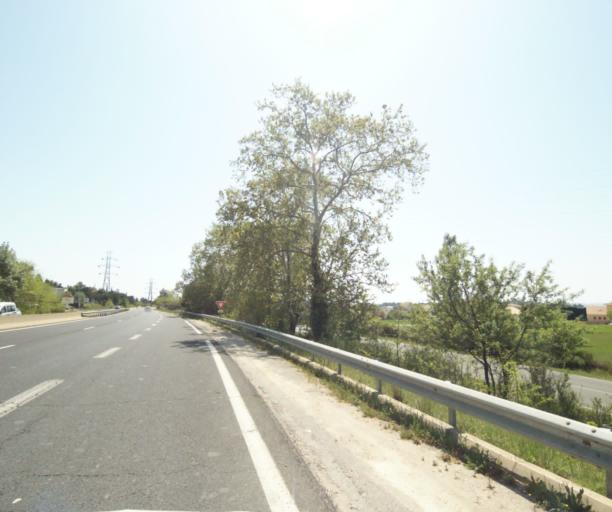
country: FR
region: Languedoc-Roussillon
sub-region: Departement de l'Herault
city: Montferrier-sur-Lez
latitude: 43.6520
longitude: 3.8367
